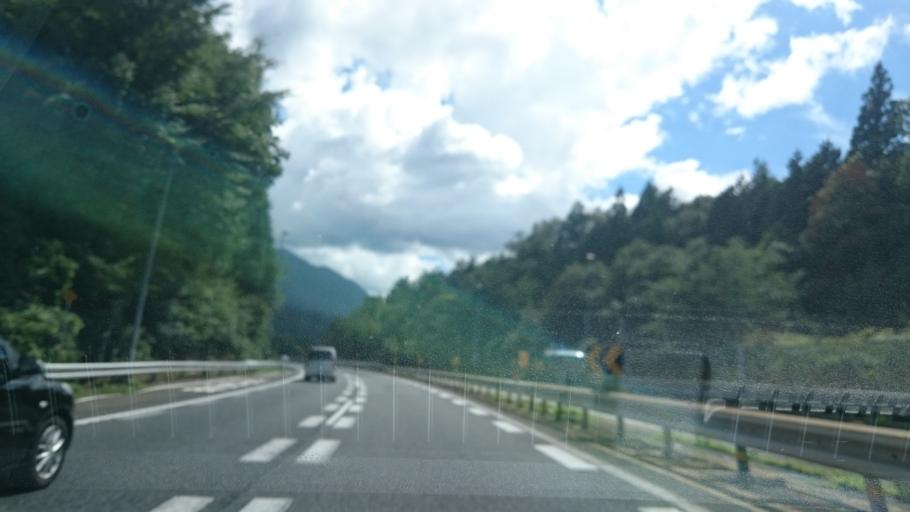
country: JP
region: Gifu
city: Nakatsugawa
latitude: 35.5166
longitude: 137.5633
